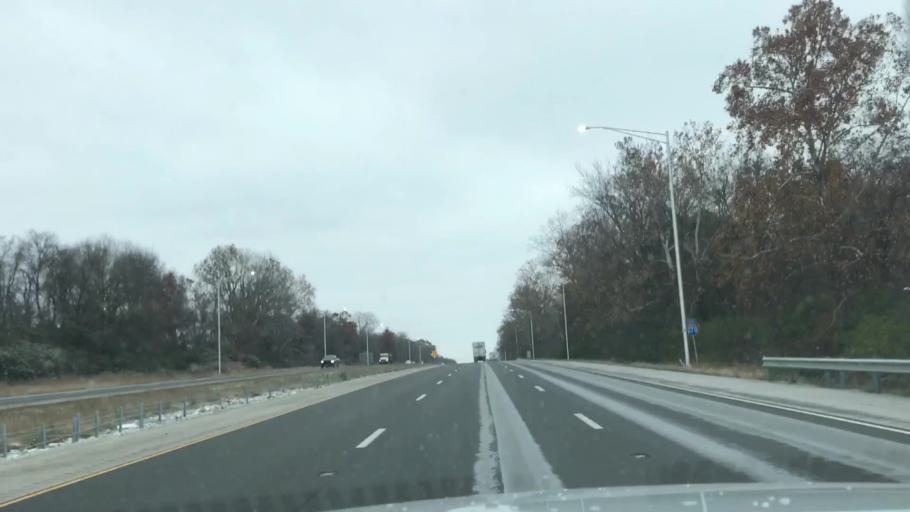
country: US
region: Illinois
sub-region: Madison County
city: Glen Carbon
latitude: 38.7566
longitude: -89.9999
